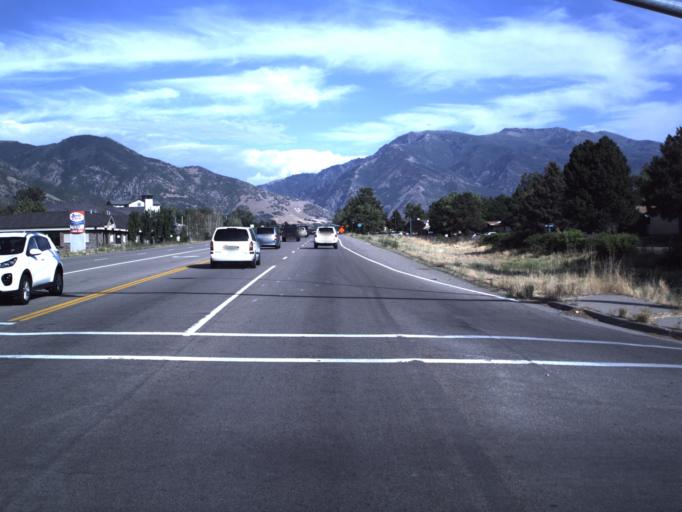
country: US
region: Utah
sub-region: Weber County
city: Washington Terrace
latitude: 41.1656
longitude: -111.9577
